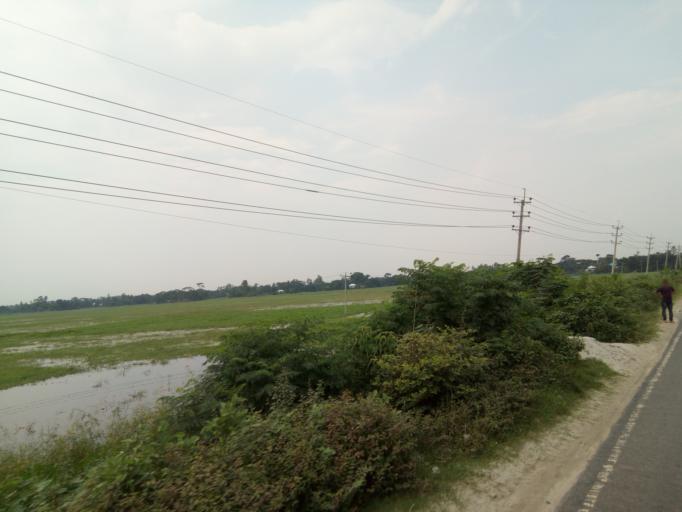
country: BD
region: Dhaka
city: Dohar
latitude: 23.5066
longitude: 90.2749
